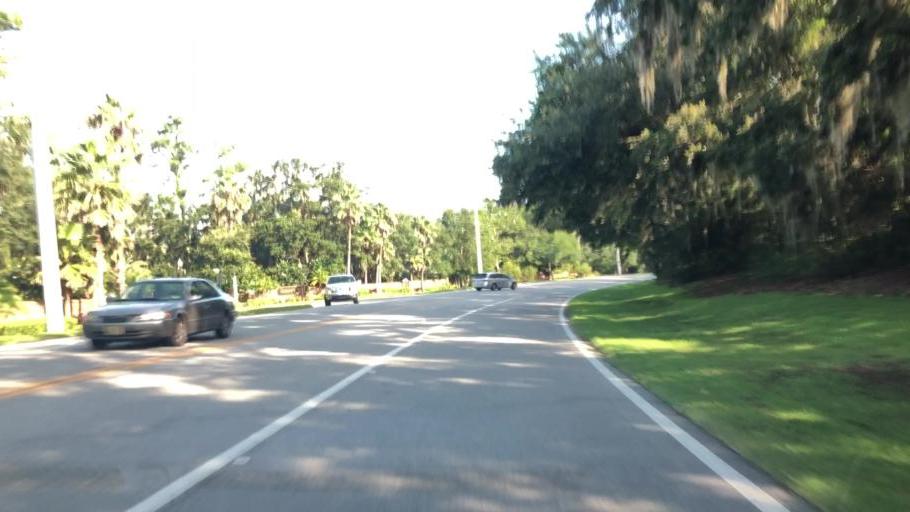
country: US
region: Florida
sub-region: Saint Johns County
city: Palm Valley
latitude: 30.1608
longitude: -81.3851
